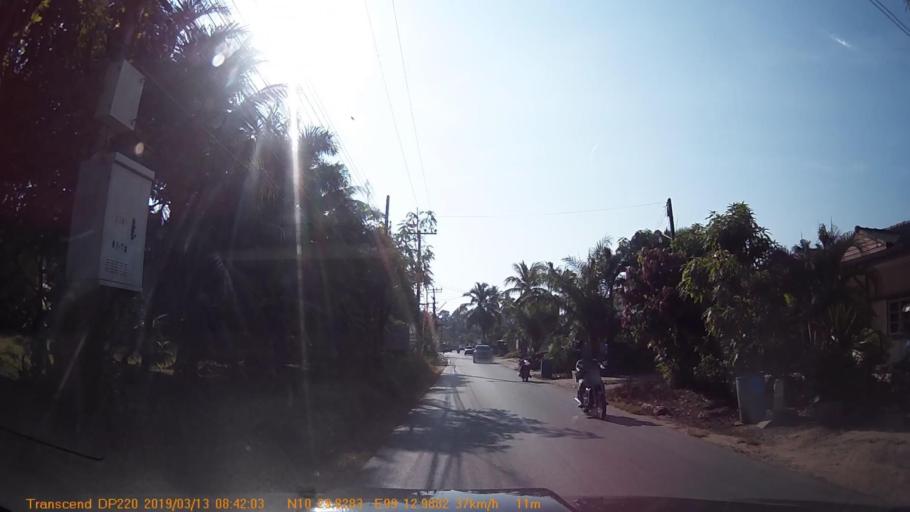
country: TH
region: Chumphon
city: Chumphon
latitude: 10.4971
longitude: 99.2166
